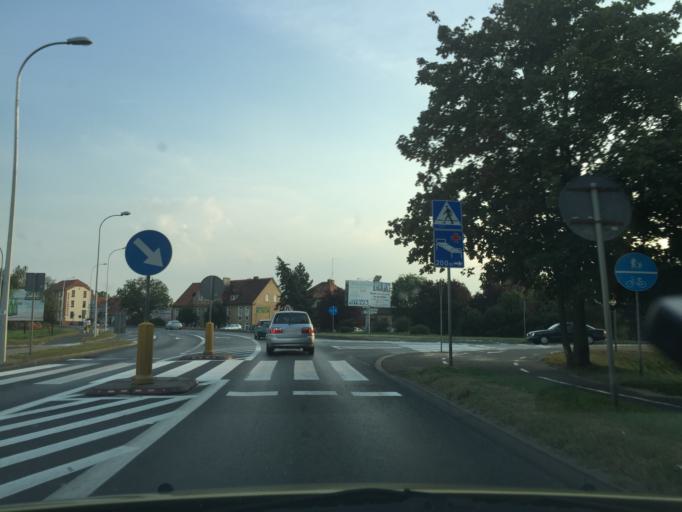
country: PL
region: Greater Poland Voivodeship
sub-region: Powiat jarocinski
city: Jarocin
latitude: 51.9685
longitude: 17.5060
